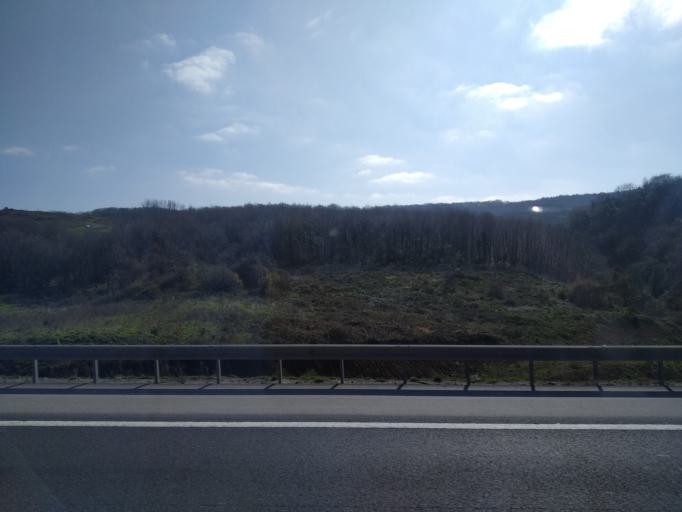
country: TR
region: Istanbul
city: Arikoey
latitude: 41.2209
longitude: 29.0059
